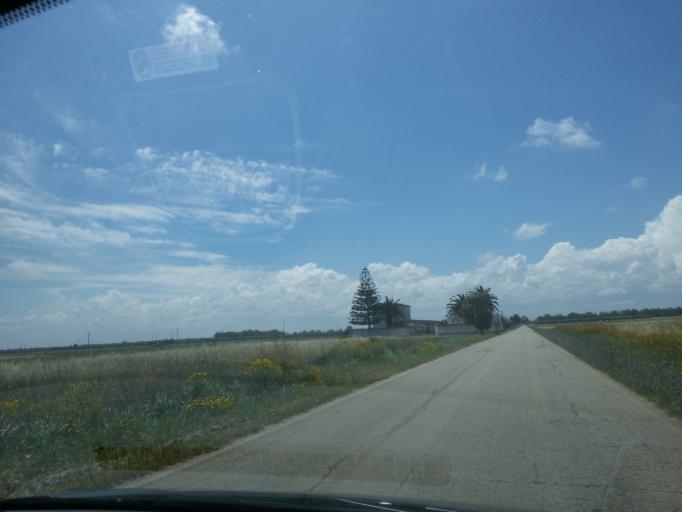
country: IT
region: Apulia
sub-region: Provincia di Brindisi
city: Brindisi
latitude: 40.6586
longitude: 17.8399
